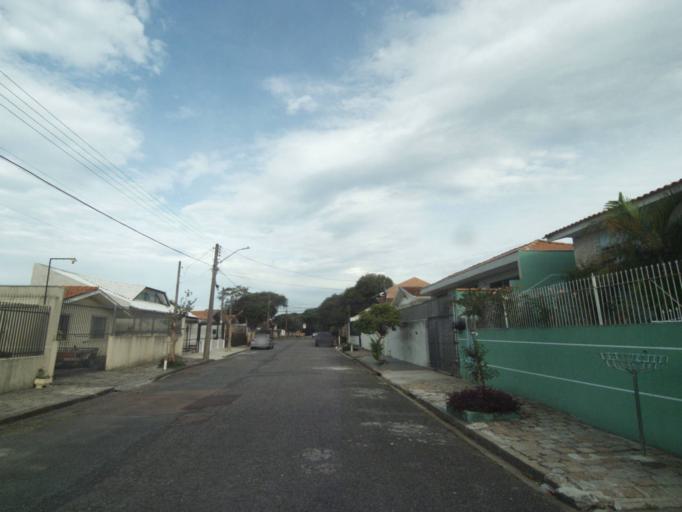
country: BR
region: Parana
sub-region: Curitiba
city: Curitiba
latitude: -25.4302
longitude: -49.2348
